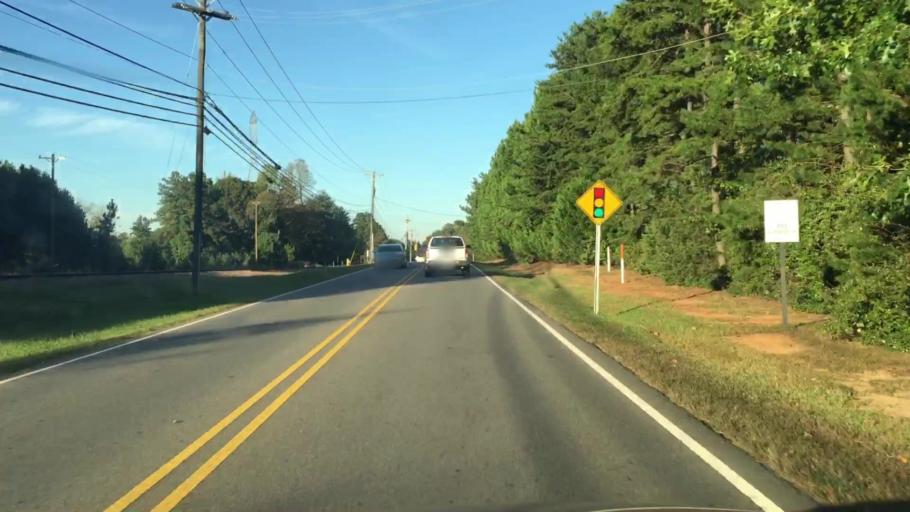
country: US
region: North Carolina
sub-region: Iredell County
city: Mooresville
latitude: 35.5627
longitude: -80.8316
